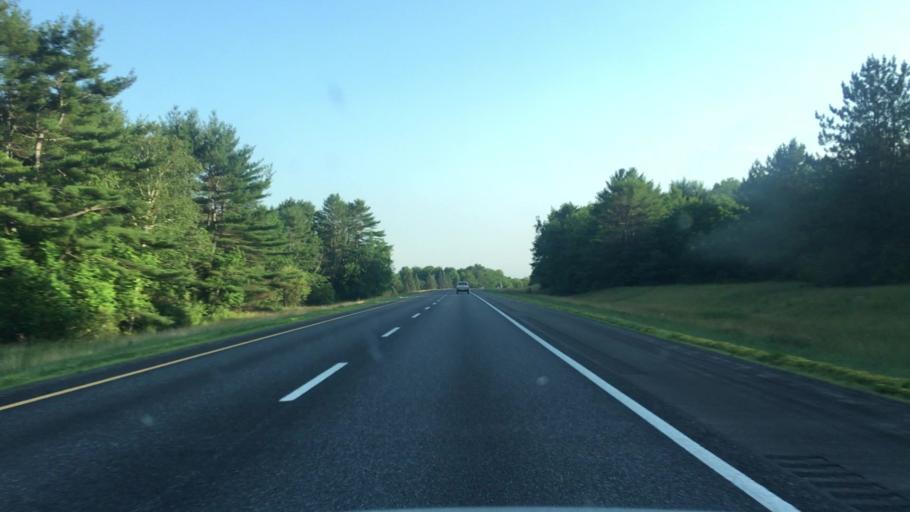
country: US
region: Maine
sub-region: Sagadahoc County
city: Richmond
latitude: 44.0694
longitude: -69.8817
